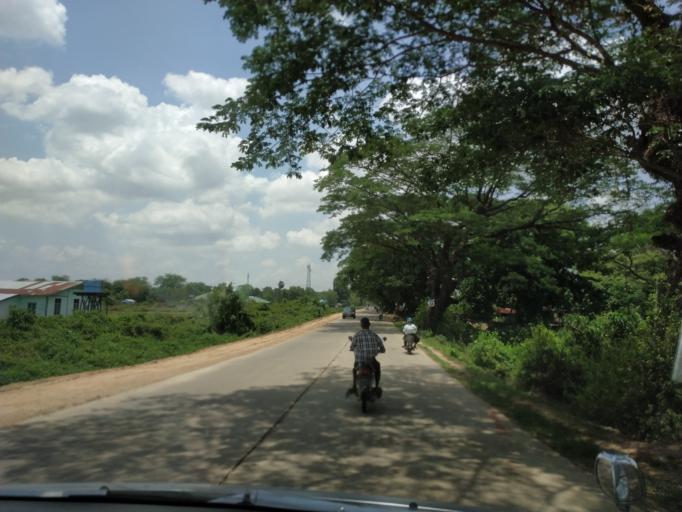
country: MM
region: Bago
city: Bago
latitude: 17.4765
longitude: 96.5110
